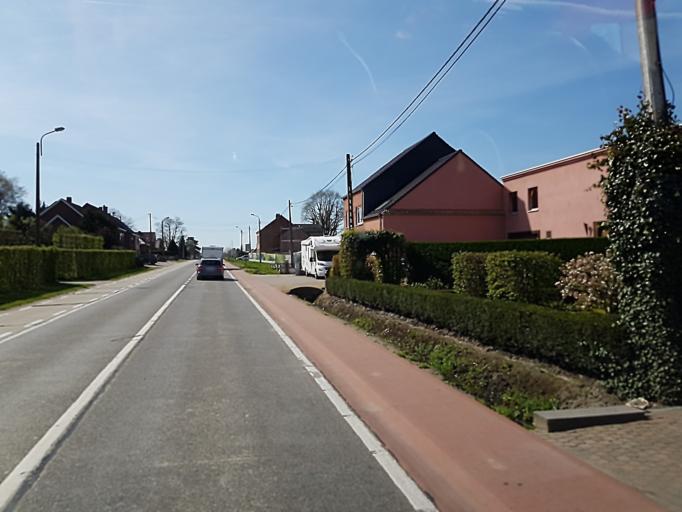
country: BE
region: Flanders
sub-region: Provincie Vlaams-Brabant
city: Aarschot
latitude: 51.0085
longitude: 4.8382
